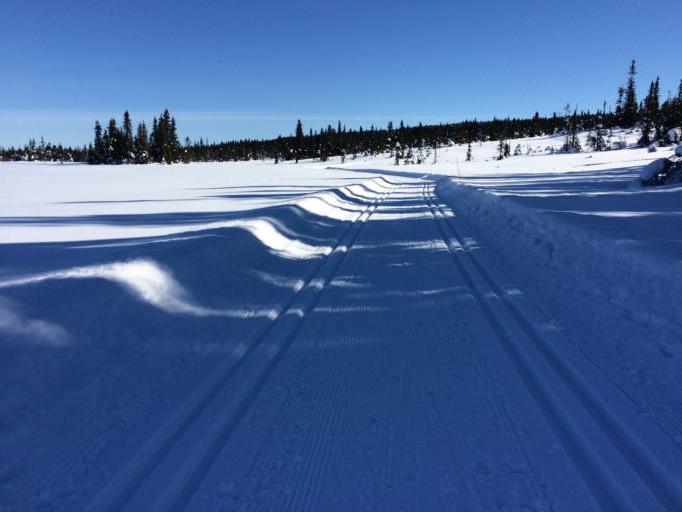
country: NO
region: Oppland
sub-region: Gausdal
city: Segalstad bru
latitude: 61.3262
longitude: 10.0842
